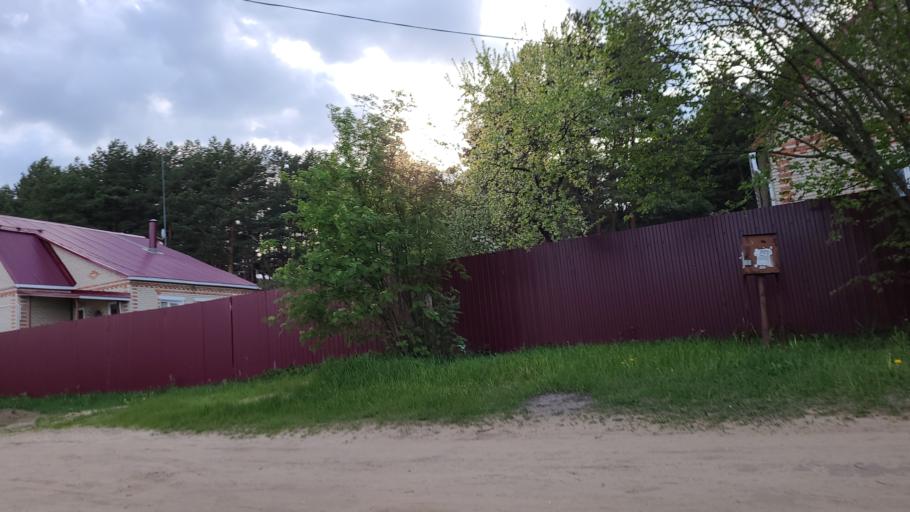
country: RU
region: Moskovskaya
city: Kratovo
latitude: 55.5566
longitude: 38.1864
